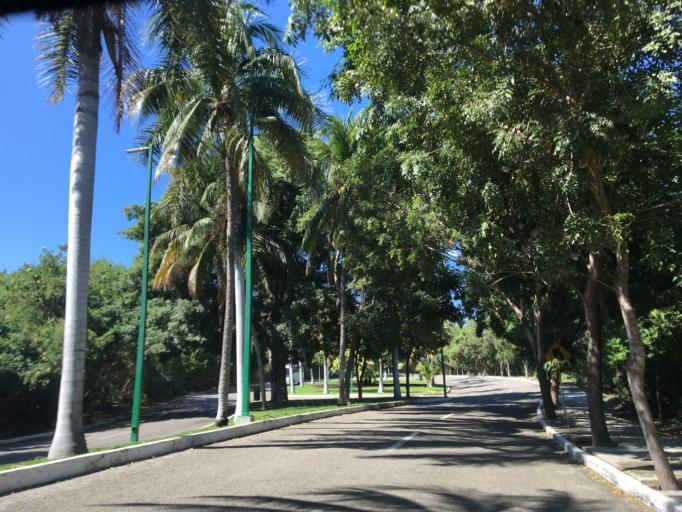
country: MX
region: Oaxaca
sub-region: Santa Maria Huatulco
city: Crucecita
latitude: 15.7750
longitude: -96.1045
